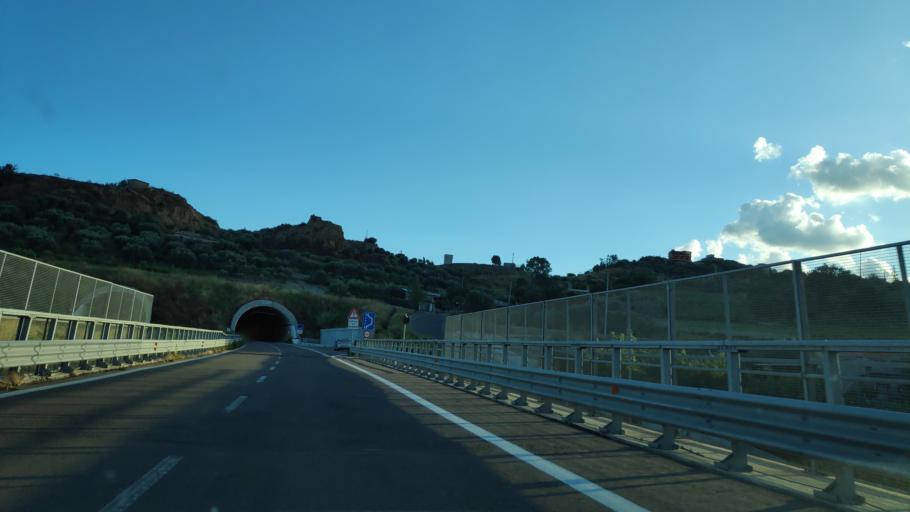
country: IT
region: Calabria
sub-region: Provincia di Reggio Calabria
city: Siderno
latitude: 38.2897
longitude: 16.2799
